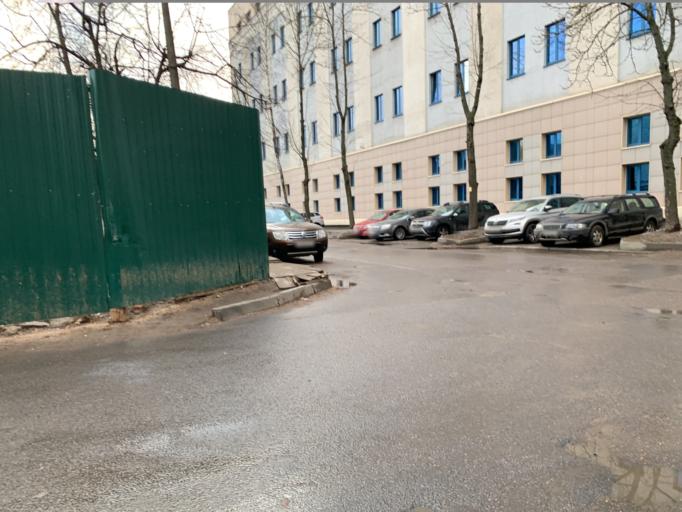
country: BY
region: Minsk
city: Minsk
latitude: 53.8894
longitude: 27.5370
